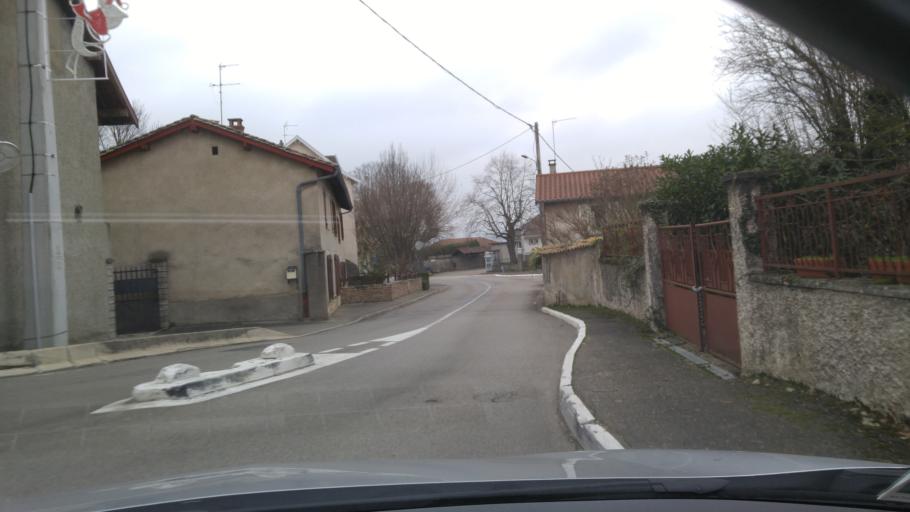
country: FR
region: Rhone-Alpes
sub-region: Departement de l'Isere
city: Charvieu-Chavagneux
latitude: 45.7279
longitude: 5.1441
